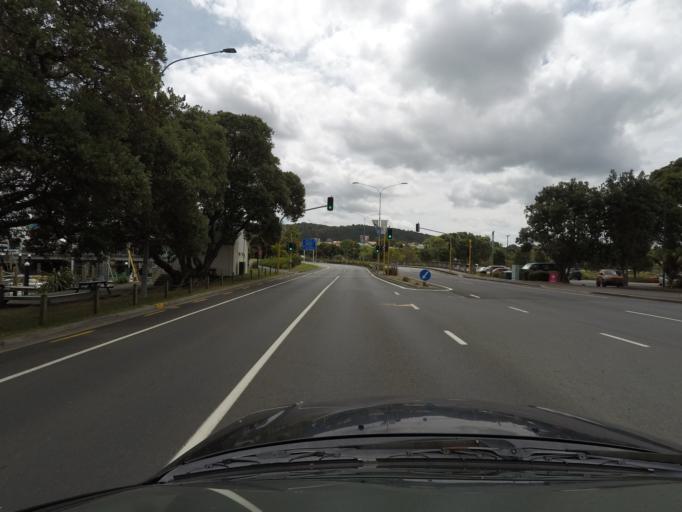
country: NZ
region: Northland
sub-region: Whangarei
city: Whangarei
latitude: -35.7228
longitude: 174.3260
